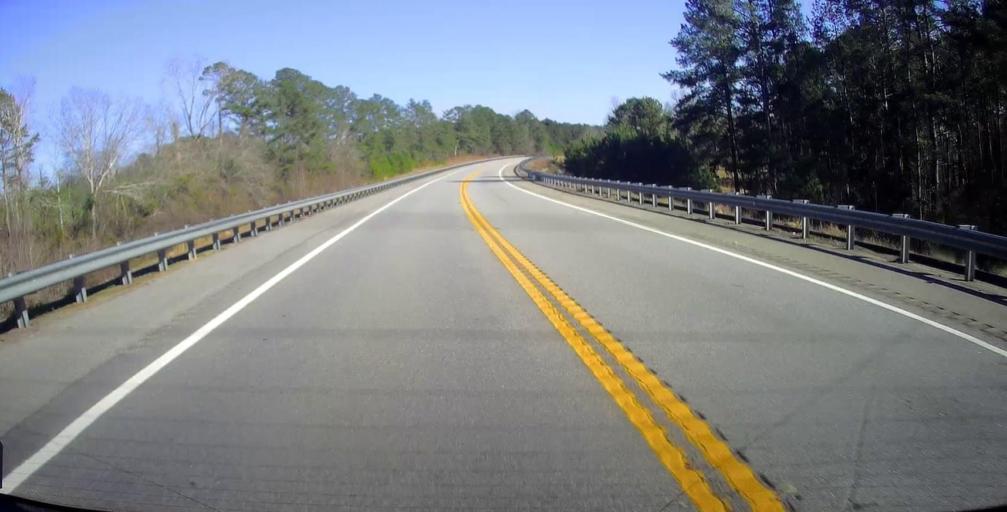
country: US
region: Georgia
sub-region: Macon County
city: Oglethorpe
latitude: 32.3451
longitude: -84.1375
